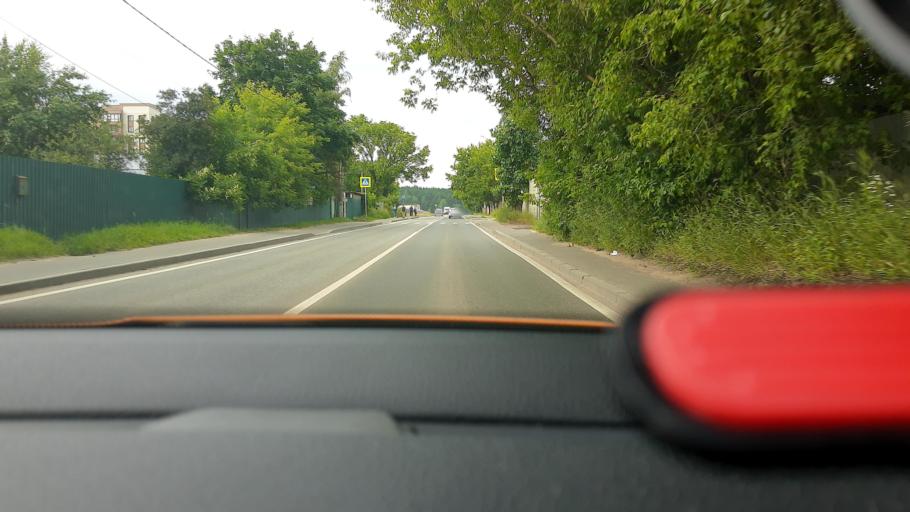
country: RU
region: Moskovskaya
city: Pirogovskiy
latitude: 55.9843
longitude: 37.7271
